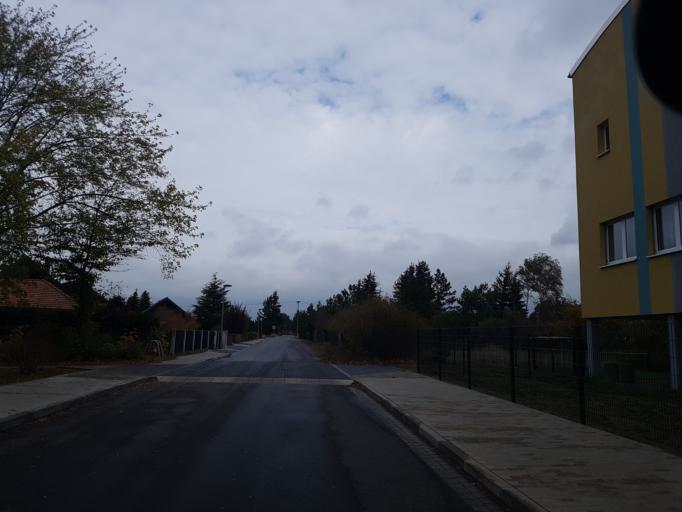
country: DE
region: Brandenburg
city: Herzberg
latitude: 51.6977
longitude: 13.2384
